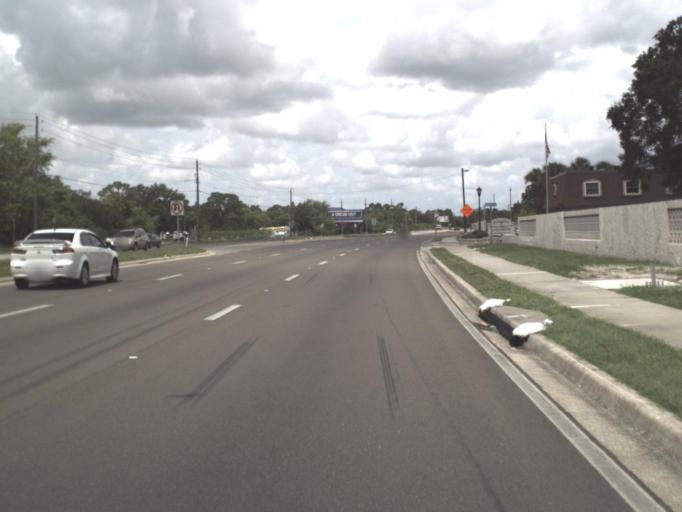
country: US
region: Florida
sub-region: Hillsborough County
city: Town 'n' Country
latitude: 27.9981
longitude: -82.5886
